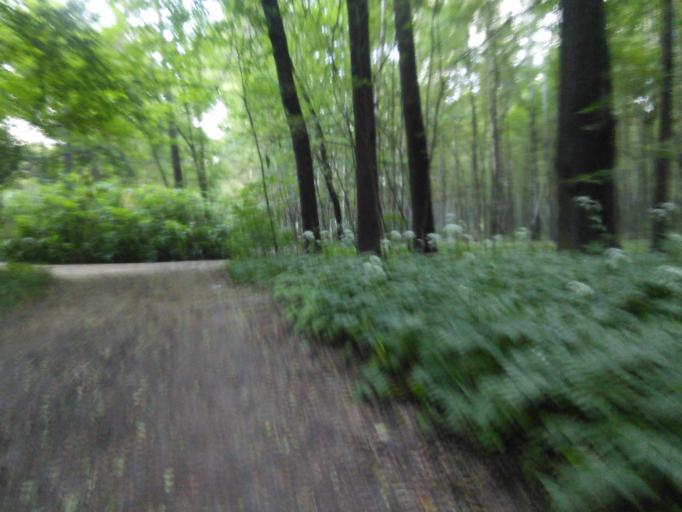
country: RU
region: Moscow
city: Sokol'niki
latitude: 55.8131
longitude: 37.6767
